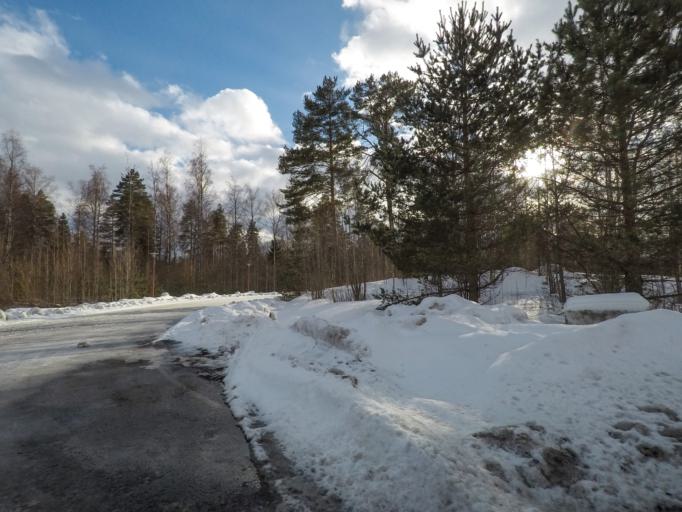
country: FI
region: Southern Savonia
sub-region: Mikkeli
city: Maentyharju
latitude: 61.4413
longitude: 26.6815
